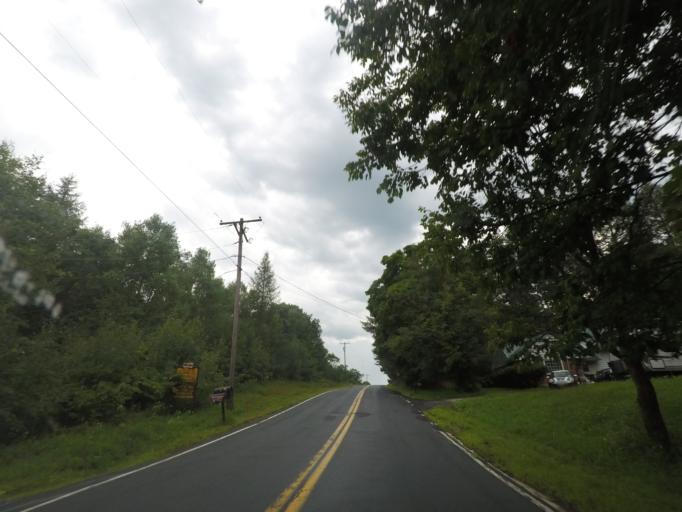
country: US
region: New York
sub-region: Rensselaer County
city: Poestenkill
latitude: 42.7515
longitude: -73.5919
